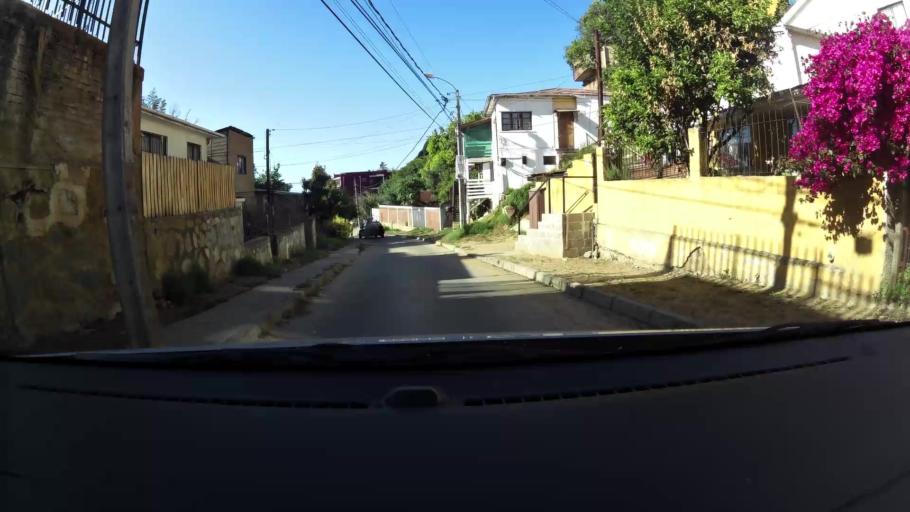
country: CL
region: Valparaiso
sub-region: Provincia de Valparaiso
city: Vina del Mar
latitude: -33.0313
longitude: -71.5609
